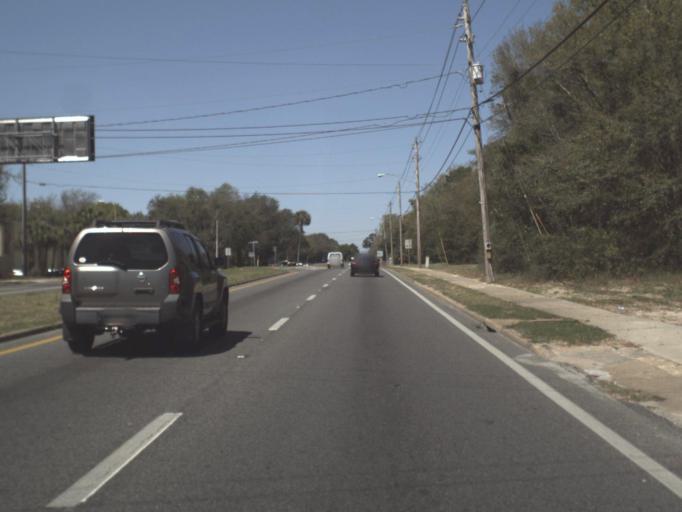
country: US
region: Florida
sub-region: Okaloosa County
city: Mary Esther
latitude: 30.4098
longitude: -86.6655
